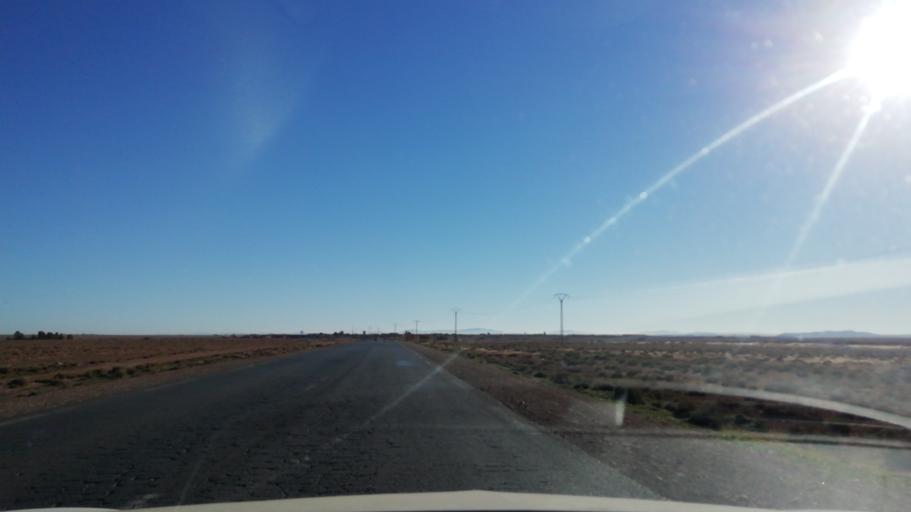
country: DZ
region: El Bayadh
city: El Bayadh
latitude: 33.8541
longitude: 0.6104
